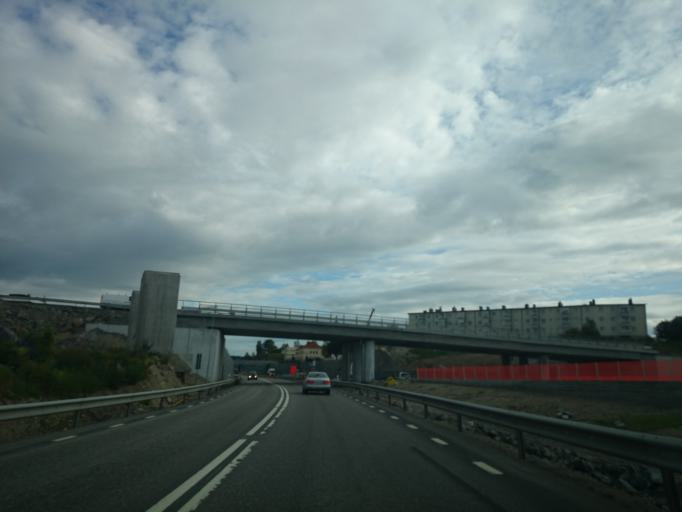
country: SE
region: Vaesternorrland
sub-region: Sundsvalls Kommun
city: Sundsvall
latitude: 62.3978
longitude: 17.3365
